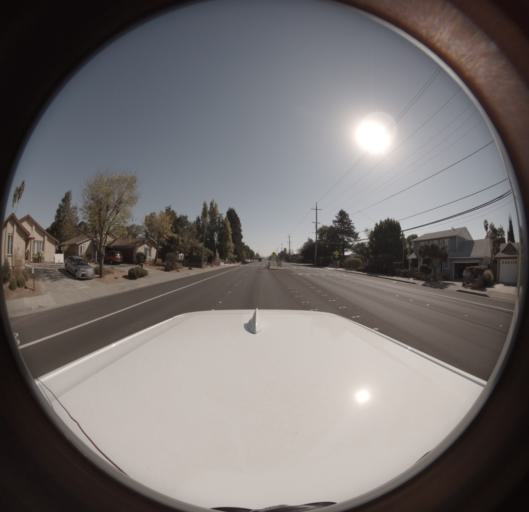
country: US
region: California
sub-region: Sonoma County
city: Petaluma
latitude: 38.2523
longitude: -122.6115
